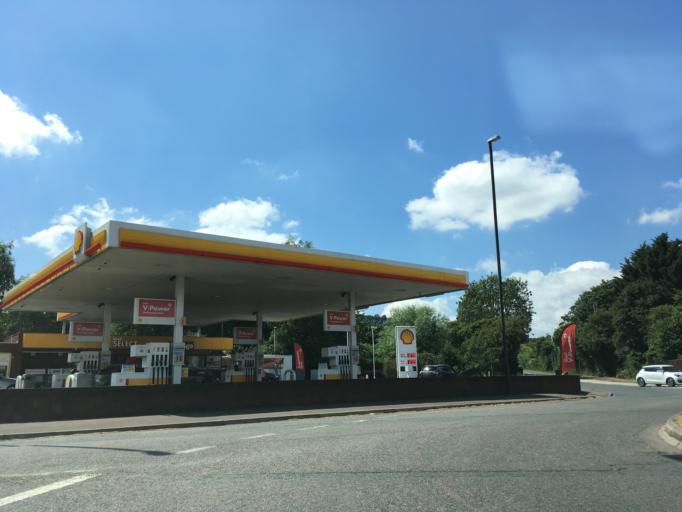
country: GB
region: England
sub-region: Gloucestershire
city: Shurdington
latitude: 51.8424
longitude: -2.1489
